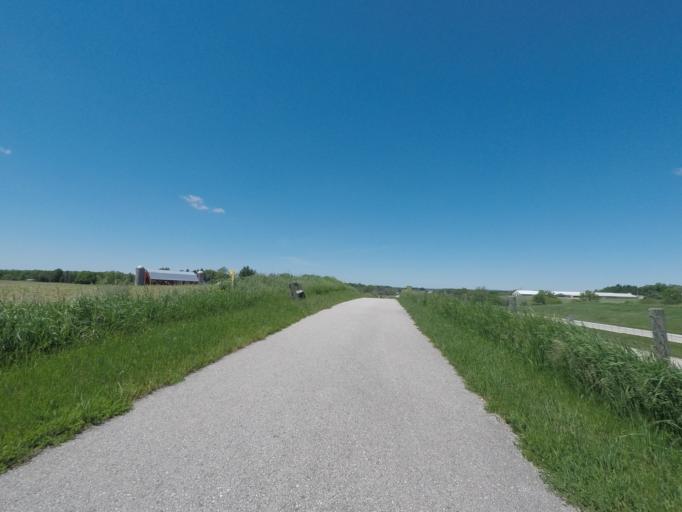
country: US
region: Wisconsin
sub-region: Sheboygan County
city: Sheboygan Falls
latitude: 43.7504
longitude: -87.8354
